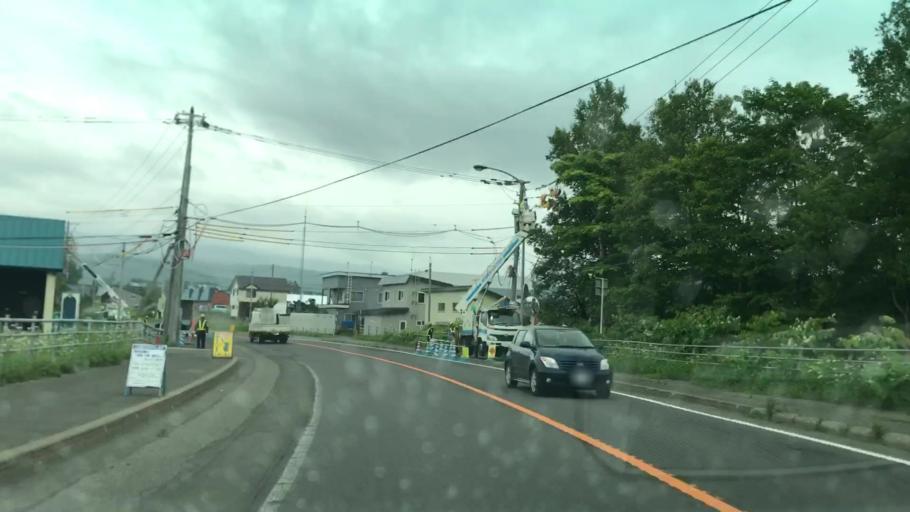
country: JP
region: Hokkaido
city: Niseko Town
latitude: 42.8098
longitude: 140.5406
